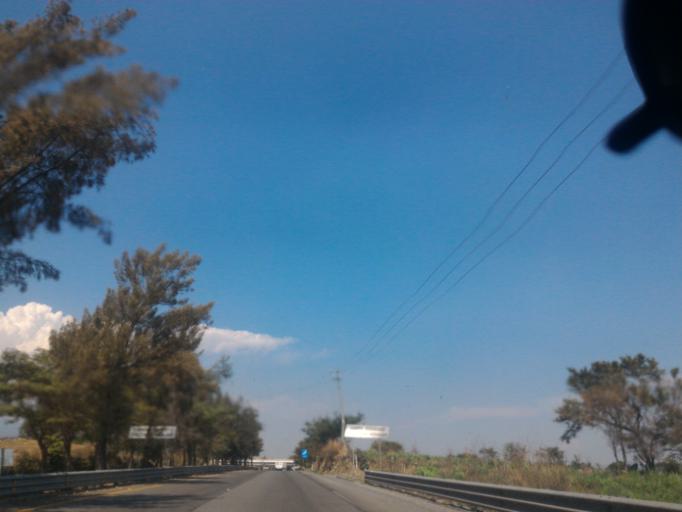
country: MX
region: Colima
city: Queseria
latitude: 19.3749
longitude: -103.5592
